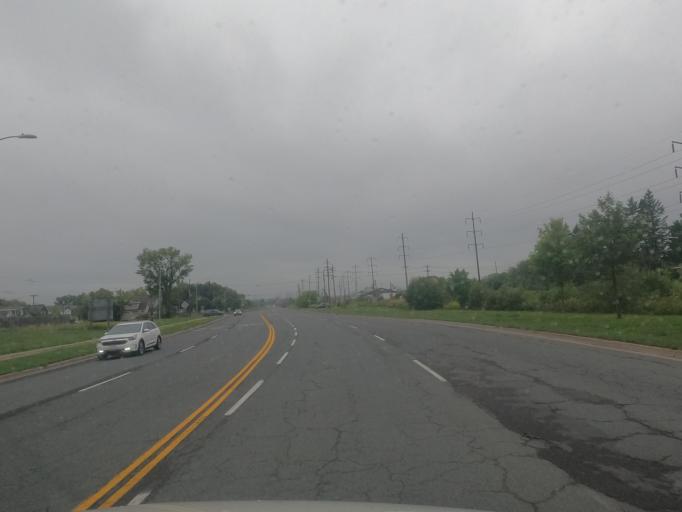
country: CA
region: Ontario
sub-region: Algoma
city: Sault Ste. Marie
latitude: 46.5333
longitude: -84.3465
